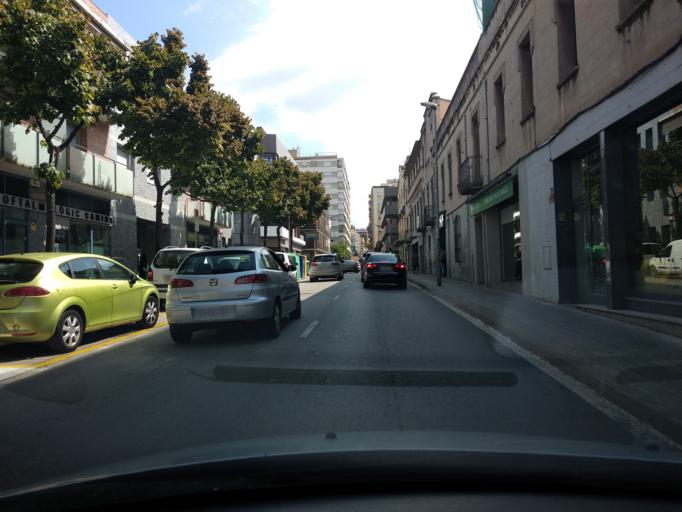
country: ES
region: Catalonia
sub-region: Provincia de Barcelona
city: Granollers
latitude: 41.6104
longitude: 2.2884
